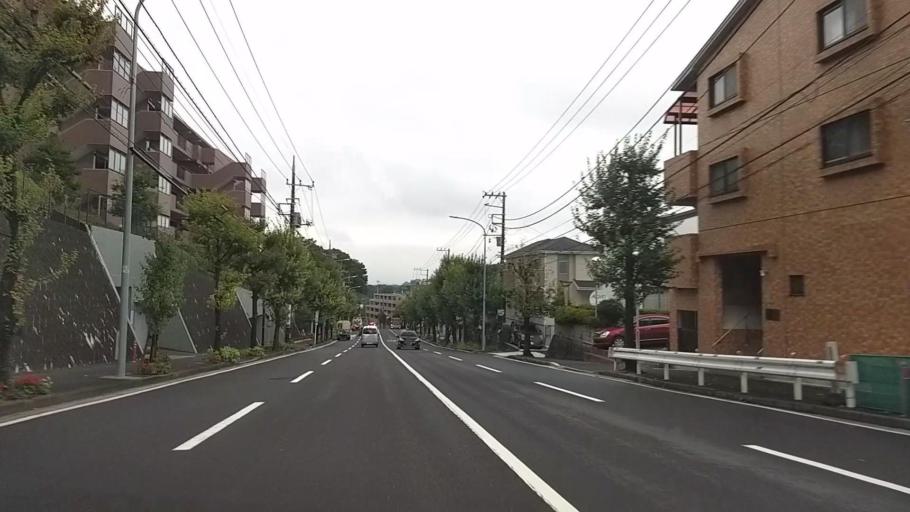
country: JP
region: Kanagawa
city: Kamakura
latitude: 35.3996
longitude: 139.5590
